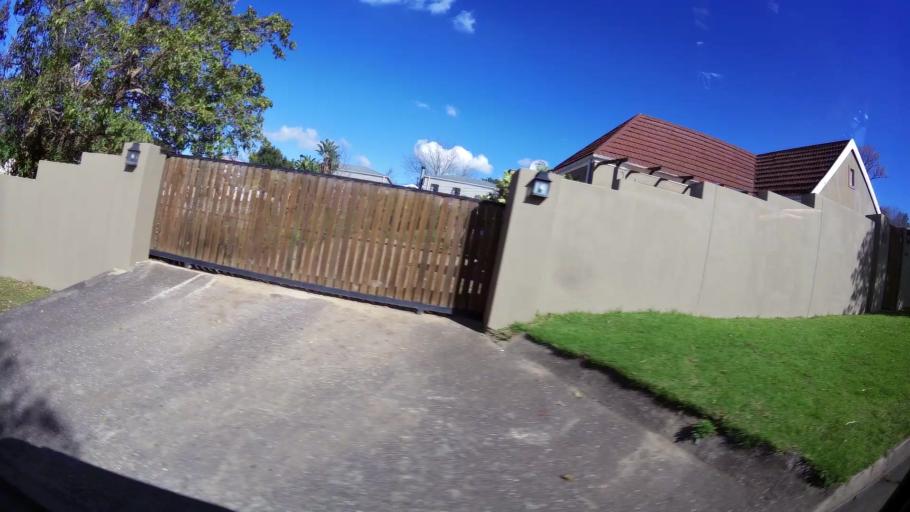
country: ZA
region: Western Cape
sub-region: Eden District Municipality
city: George
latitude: -33.9509
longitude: 22.4695
